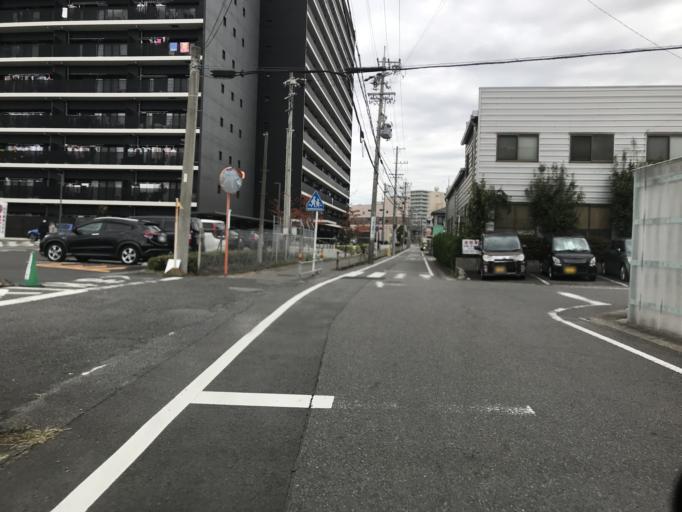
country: JP
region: Aichi
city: Nagoya-shi
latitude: 35.1960
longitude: 136.8599
